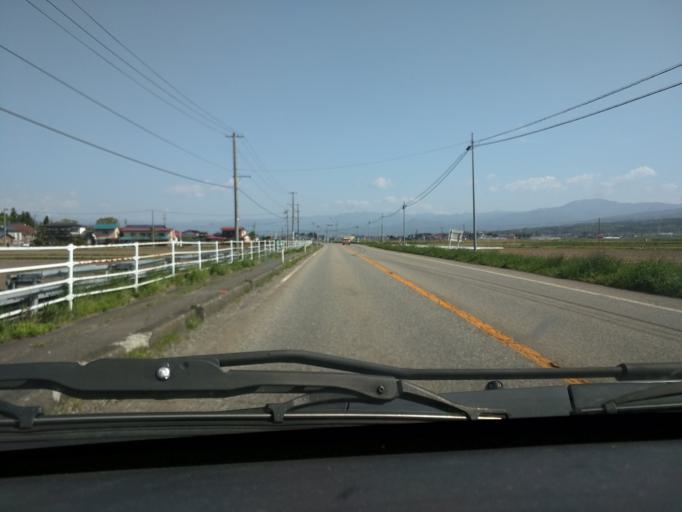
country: JP
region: Fukushima
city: Kitakata
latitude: 37.5596
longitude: 139.9068
